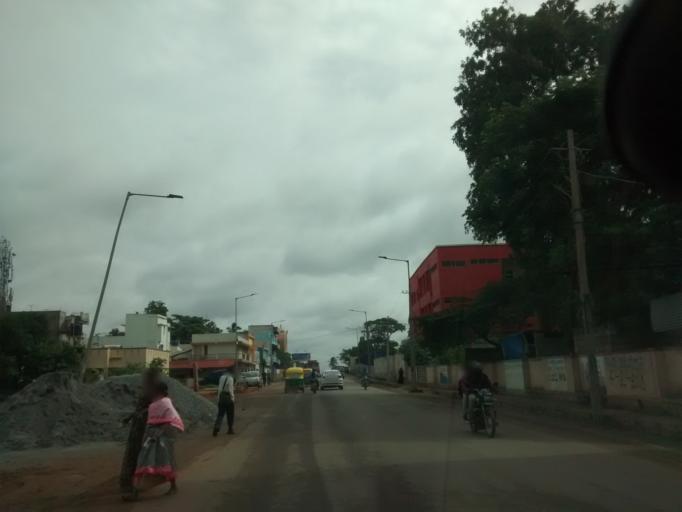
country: IN
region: Karnataka
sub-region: Tumkur
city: Tumkur
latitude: 13.3456
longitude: 77.1018
